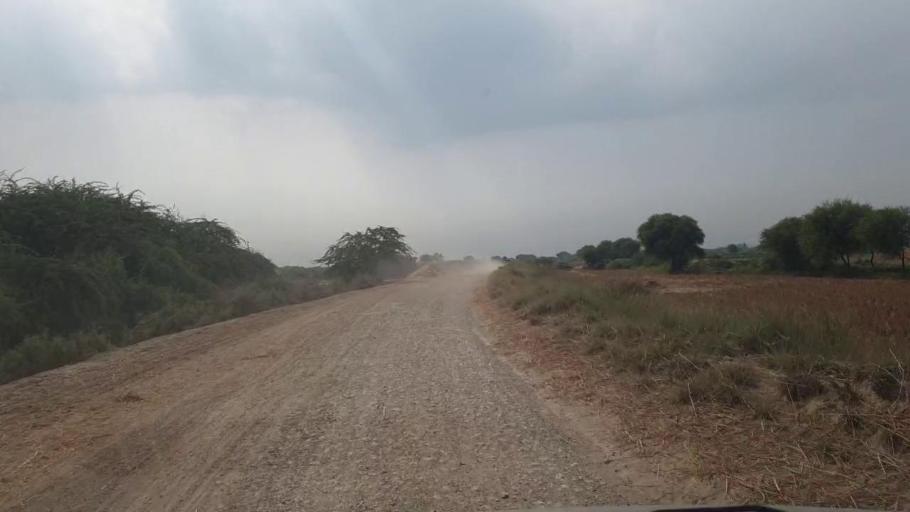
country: PK
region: Sindh
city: Talhar
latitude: 24.9282
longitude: 68.7868
